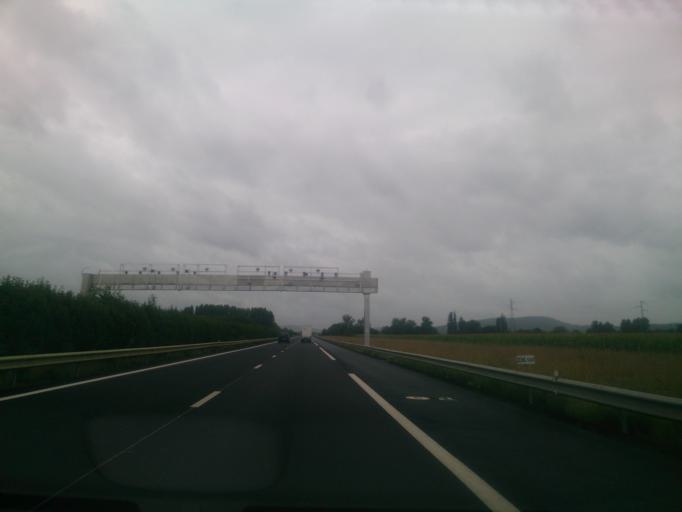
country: FR
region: Midi-Pyrenees
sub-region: Departement de la Haute-Garonne
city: Cazeres
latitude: 43.2229
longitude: 1.0509
